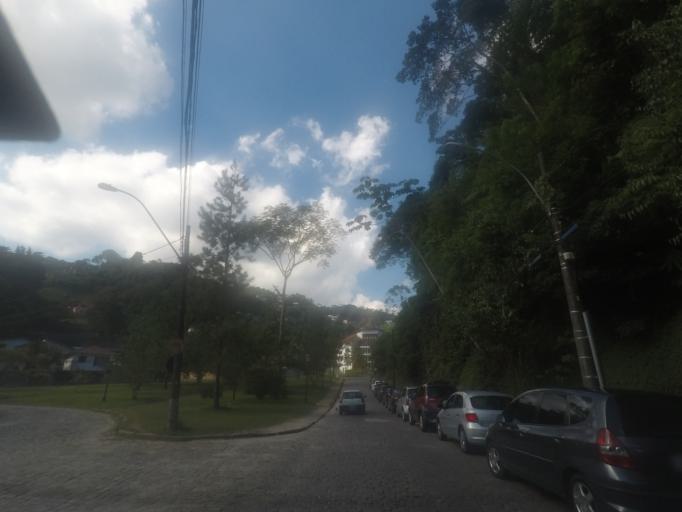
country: BR
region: Rio de Janeiro
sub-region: Petropolis
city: Petropolis
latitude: -22.5263
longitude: -43.2116
